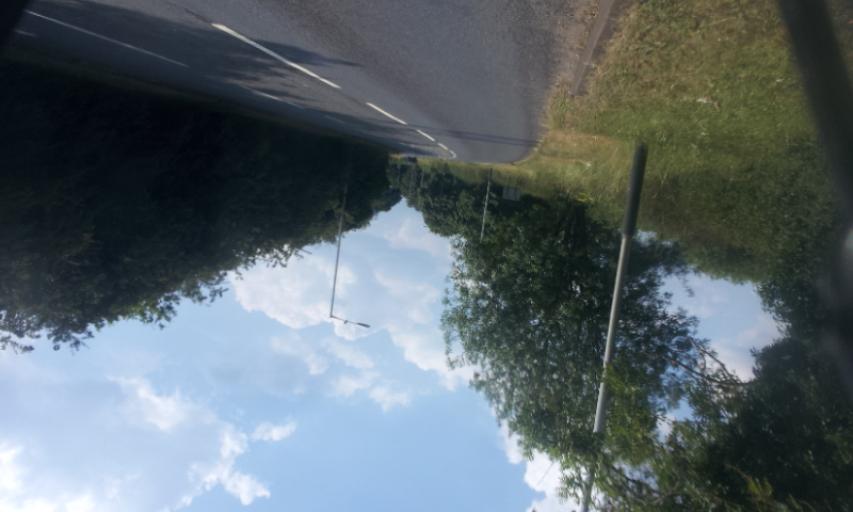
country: GB
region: England
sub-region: Kent
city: Paddock Wood
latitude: 51.1713
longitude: 0.3858
